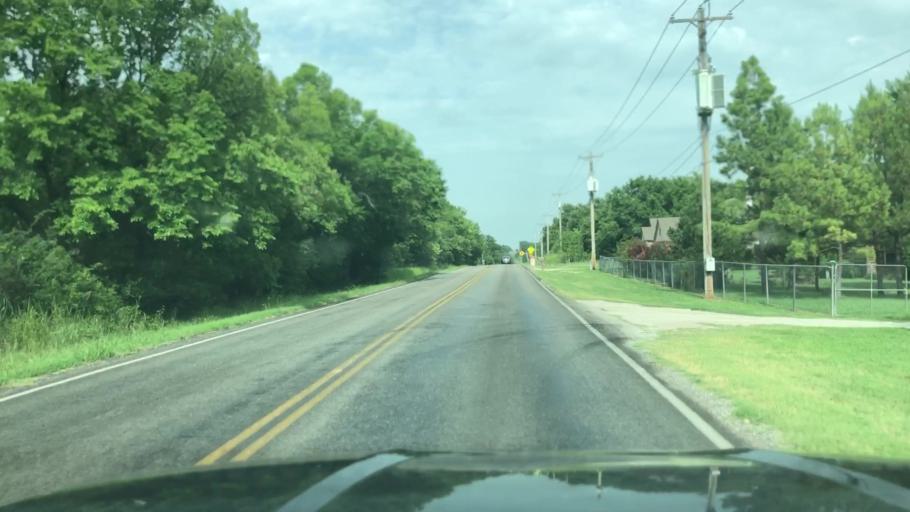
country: US
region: Oklahoma
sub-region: Tulsa County
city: Sand Springs
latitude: 36.0902
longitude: -96.1159
